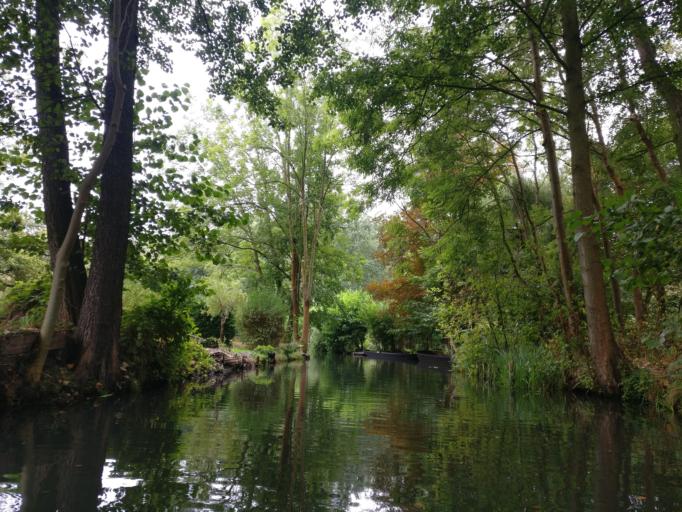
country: DE
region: Brandenburg
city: Lubbenau
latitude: 51.8677
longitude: 13.9949
